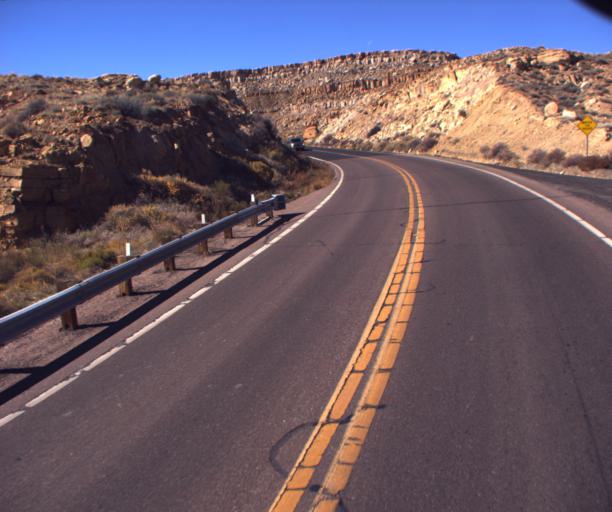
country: US
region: Arizona
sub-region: Navajo County
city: First Mesa
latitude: 35.8065
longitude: -110.5170
